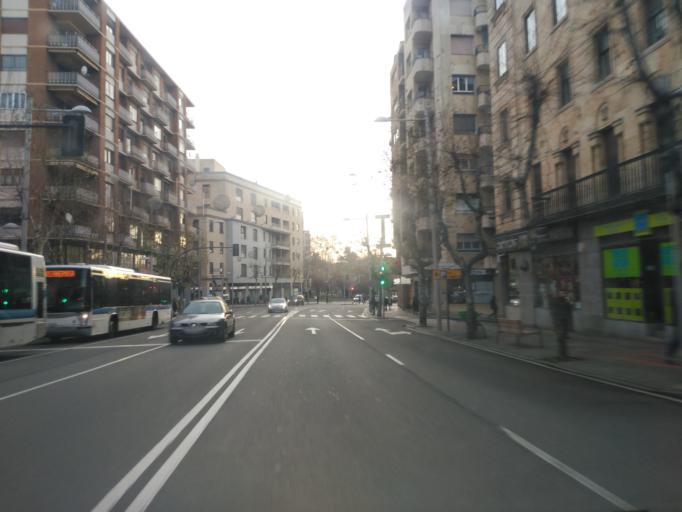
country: ES
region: Castille and Leon
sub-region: Provincia de Salamanca
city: Salamanca
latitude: 40.9694
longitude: -5.6610
